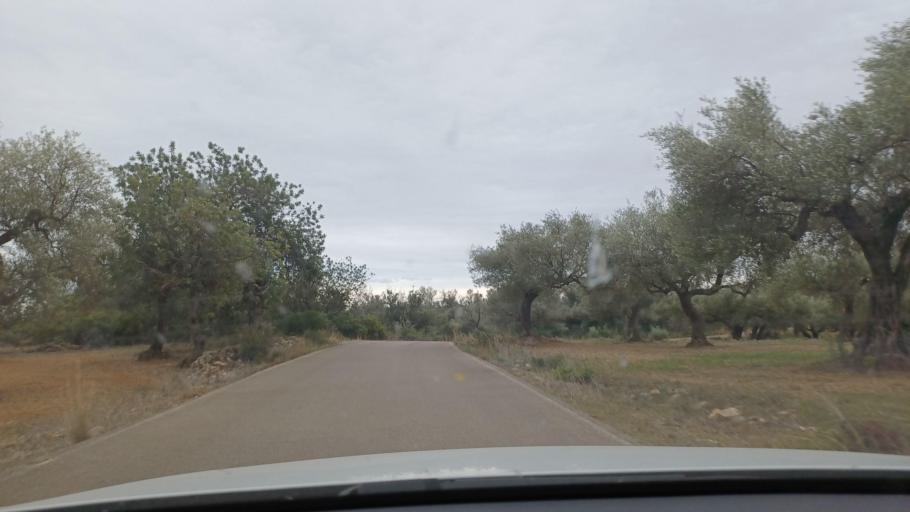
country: ES
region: Valencia
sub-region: Provincia de Castello
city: Canet lo Roig
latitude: 40.5943
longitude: 0.2839
